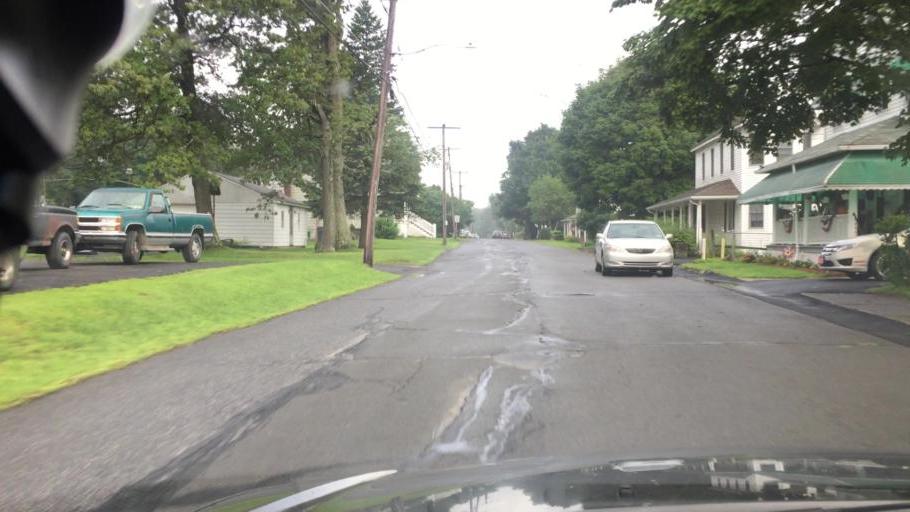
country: US
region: Pennsylvania
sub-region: Luzerne County
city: Freeland
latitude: 41.0246
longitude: -75.8993
